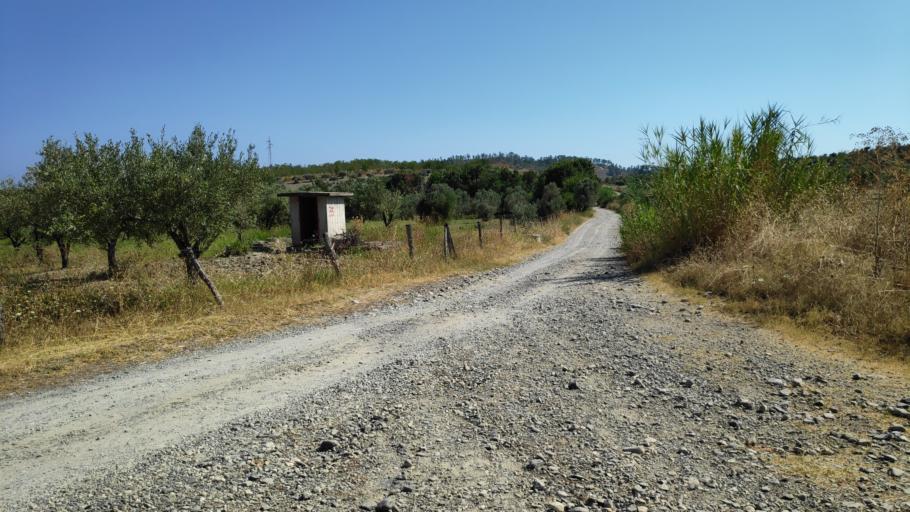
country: IT
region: Calabria
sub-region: Provincia di Reggio Calabria
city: Monasterace
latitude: 38.4356
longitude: 16.5253
